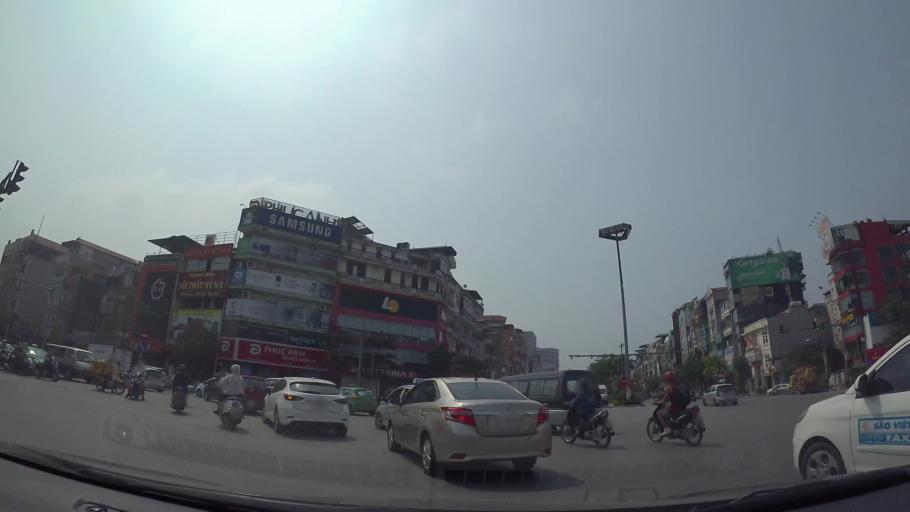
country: VN
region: Ha Noi
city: Hai BaTrung
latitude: 21.0110
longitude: 105.8372
